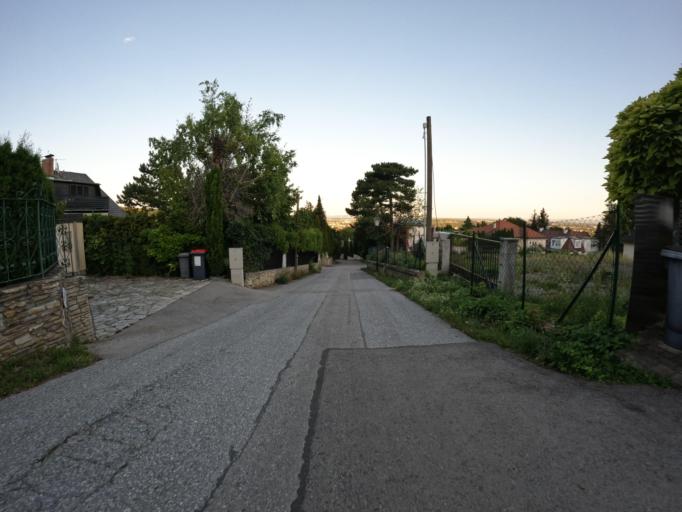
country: AT
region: Lower Austria
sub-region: Politischer Bezirk Baden
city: Baden
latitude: 48.0123
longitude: 16.2167
